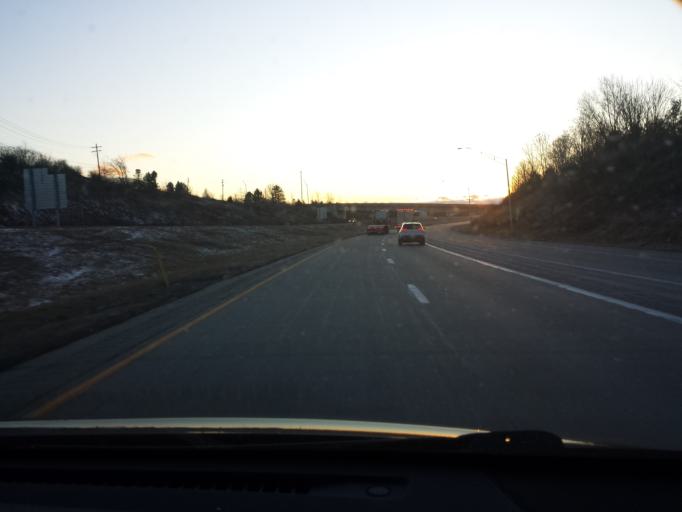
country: US
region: Pennsylvania
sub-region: Centre County
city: Pleasant Gap
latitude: 40.8856
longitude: -77.7375
